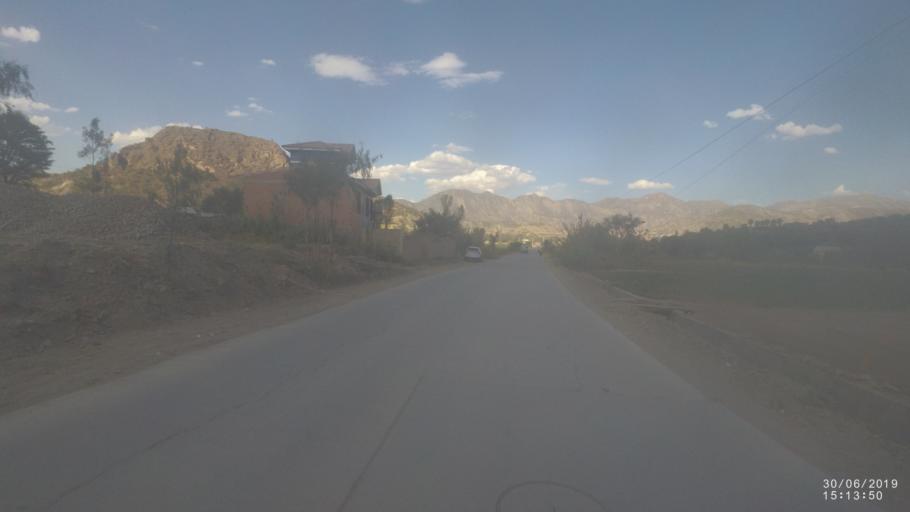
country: BO
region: Cochabamba
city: Irpa Irpa
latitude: -17.7232
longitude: -66.2803
